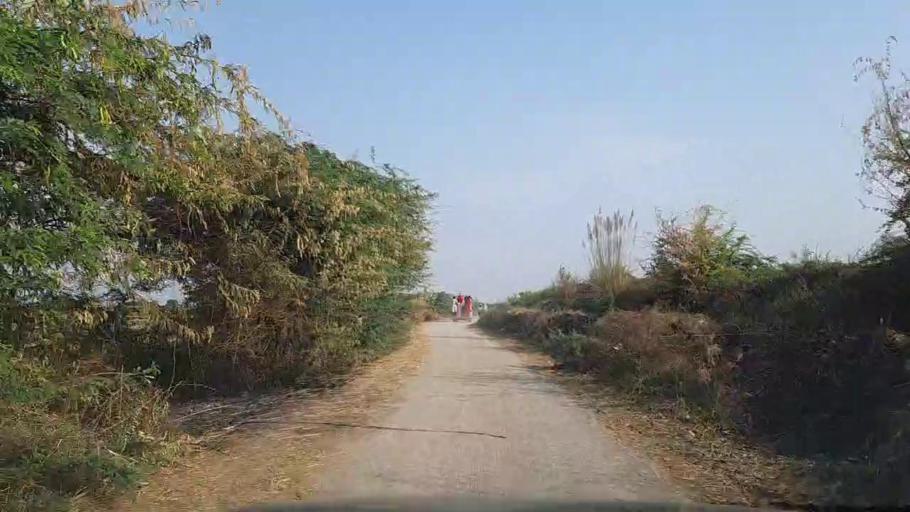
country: PK
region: Sindh
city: Thatta
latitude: 24.6481
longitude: 67.9269
